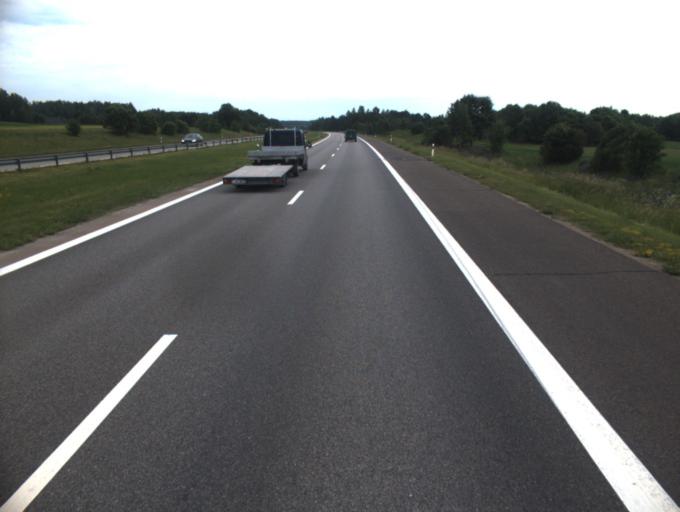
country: LT
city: Skaudvile
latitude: 55.4169
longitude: 22.7912
